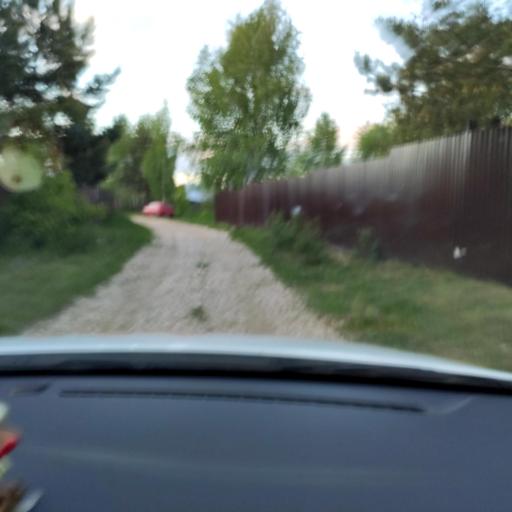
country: RU
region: Tatarstan
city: Stolbishchi
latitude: 55.5937
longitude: 49.0980
